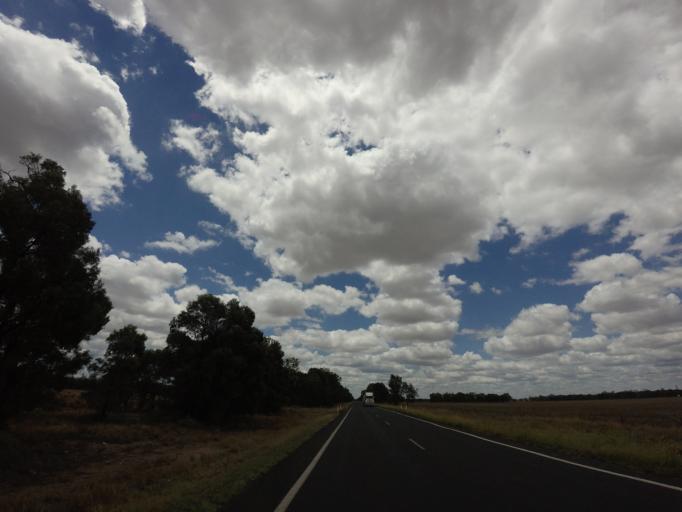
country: AU
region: Queensland
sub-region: Goondiwindi
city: Goondiwindi
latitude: -28.1380
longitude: 150.6939
